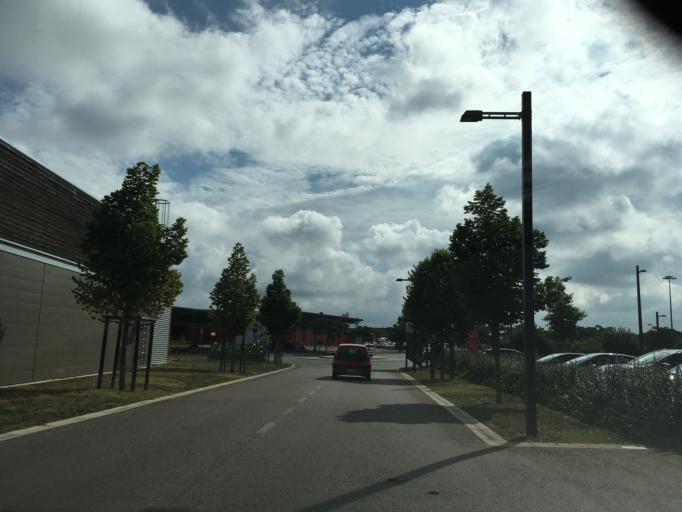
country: FR
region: Aquitaine
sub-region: Departement du Lot-et-Garonne
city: Boe
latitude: 44.1769
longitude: 0.6310
